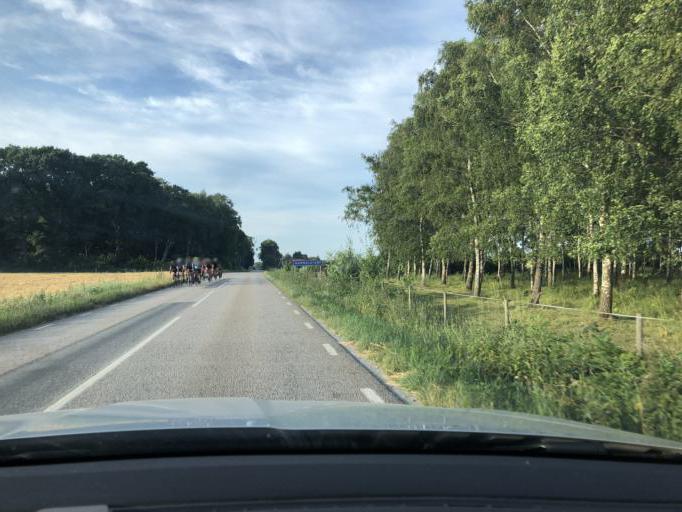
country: SE
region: Blekinge
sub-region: Solvesborgs Kommun
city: Soelvesborg
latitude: 56.0945
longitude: 14.6125
